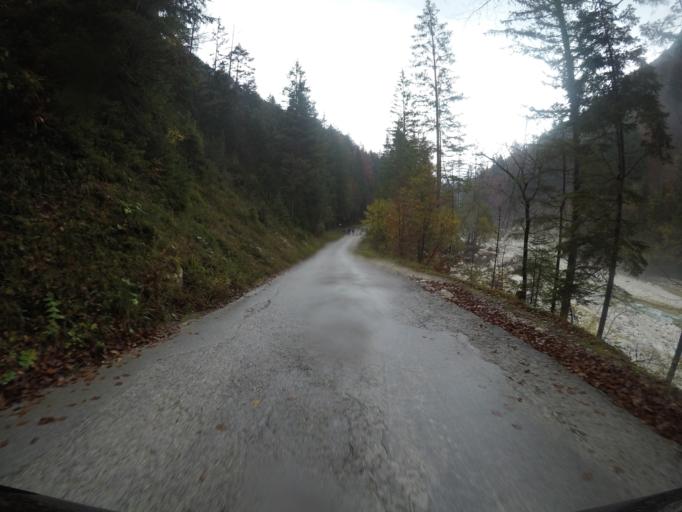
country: SI
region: Kranjska Gora
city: Mojstrana
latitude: 46.4389
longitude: 13.8966
